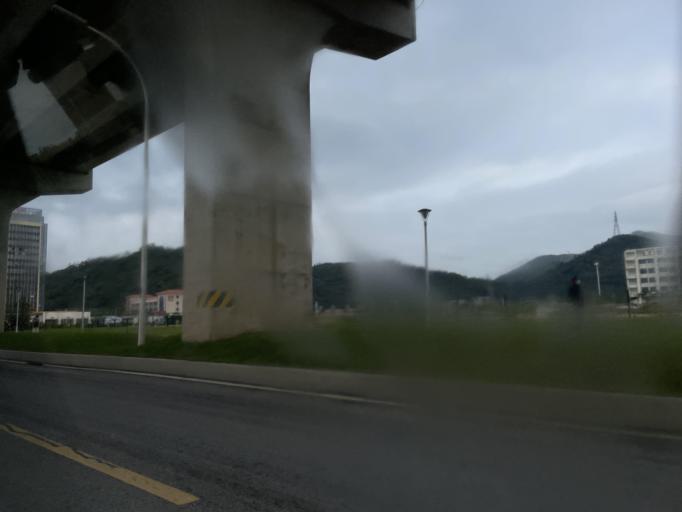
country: CN
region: Guangdong
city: Wanzai
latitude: 22.1765
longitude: 113.4858
